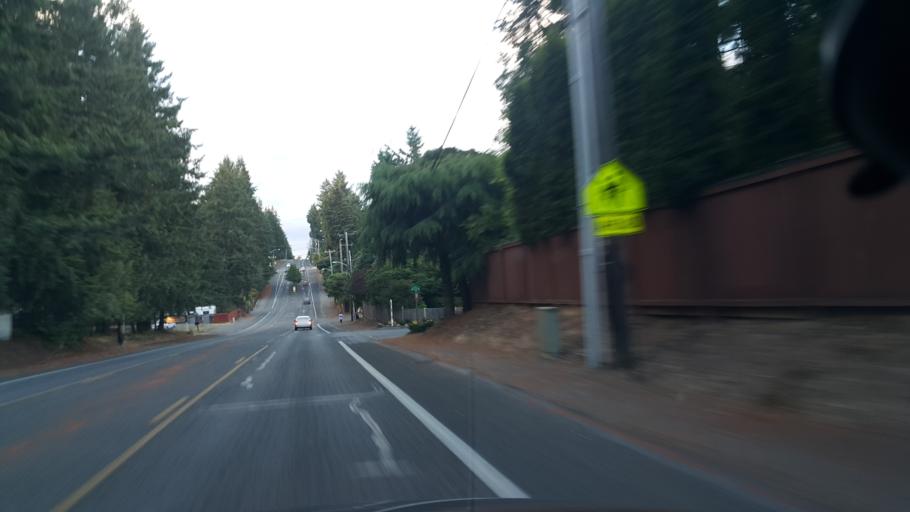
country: US
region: Washington
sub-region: Pierce County
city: Fircrest
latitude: 47.2069
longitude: -122.5266
